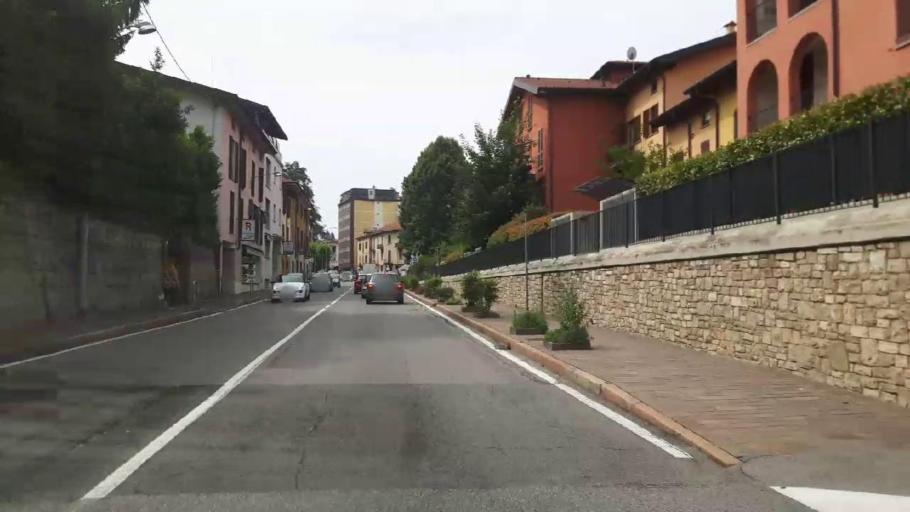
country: IT
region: Lombardy
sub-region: Provincia di Como
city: Fino Mornasco
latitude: 45.7476
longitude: 9.0501
